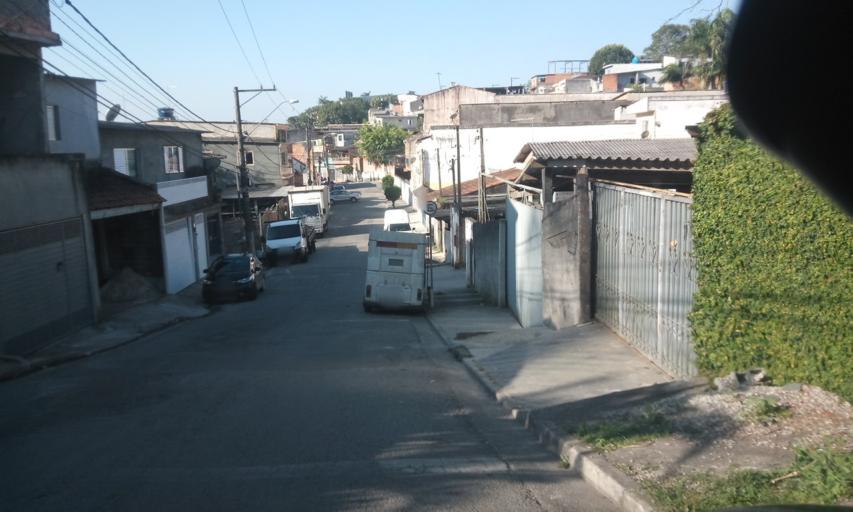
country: BR
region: Sao Paulo
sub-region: Sao Bernardo Do Campo
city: Sao Bernardo do Campo
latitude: -23.7876
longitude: -46.5266
